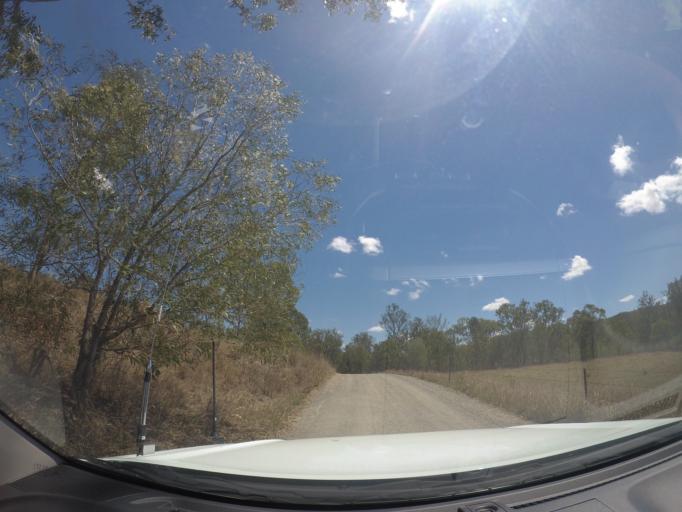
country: AU
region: Queensland
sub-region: Logan
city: North Maclean
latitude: -27.8231
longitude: 152.8592
